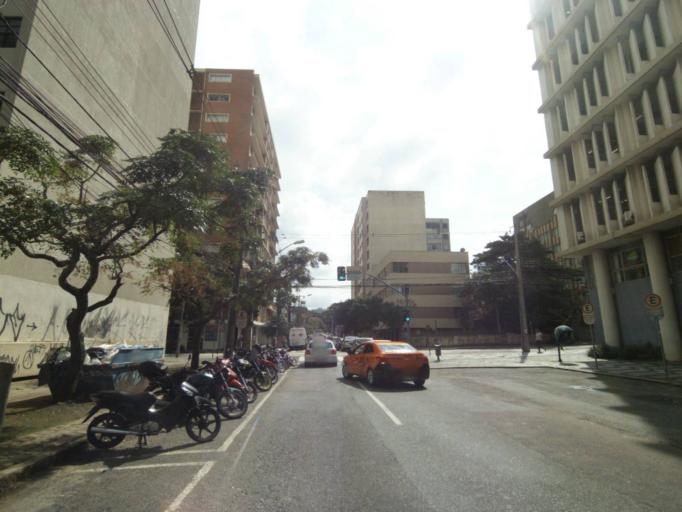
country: BR
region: Parana
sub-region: Curitiba
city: Curitiba
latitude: -25.4269
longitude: -49.2624
